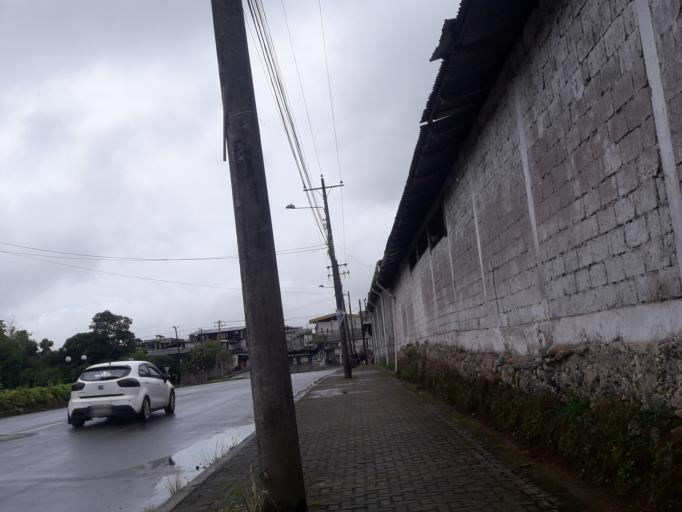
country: EC
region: Napo
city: Tena
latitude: -0.9869
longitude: -77.8144
